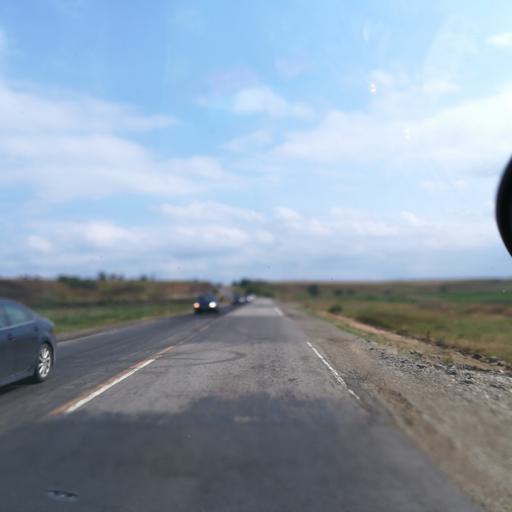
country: RU
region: Krasnodarskiy
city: Varenikovskaya
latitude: 45.1778
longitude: 37.6531
